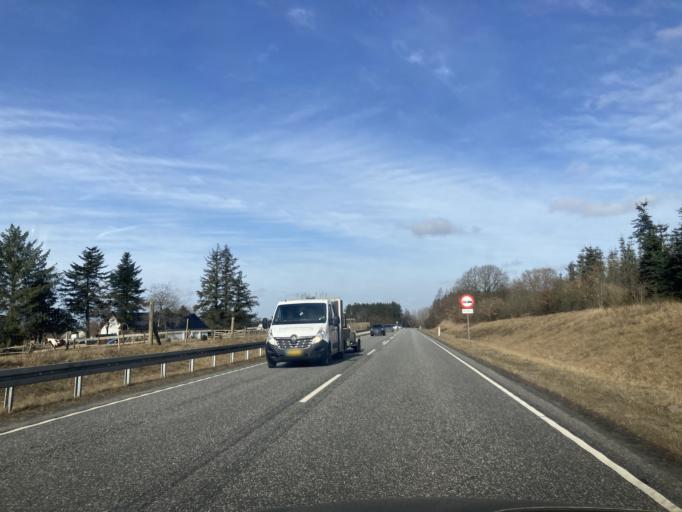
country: DK
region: Central Jutland
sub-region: Hedensted Kommune
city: Torring
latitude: 55.9733
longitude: 9.3981
